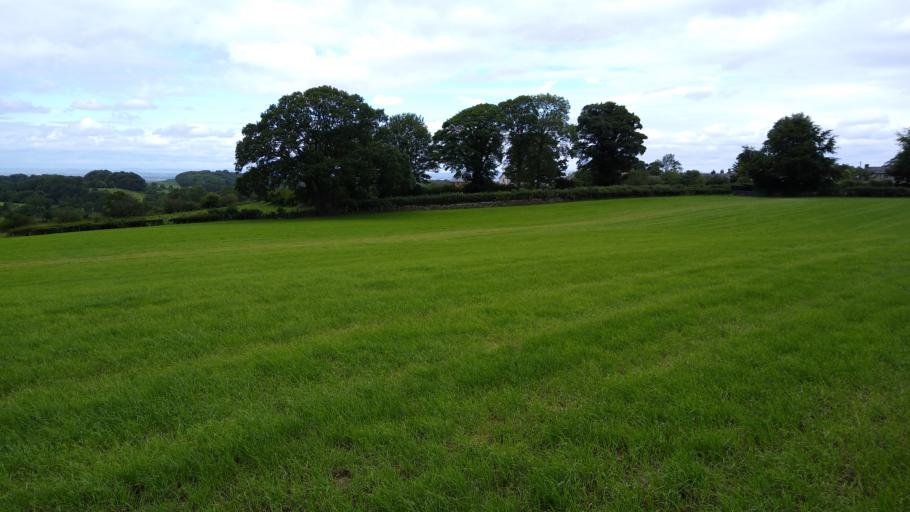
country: GB
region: England
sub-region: Cumbria
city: Brampton
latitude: 54.9073
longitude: -2.7070
